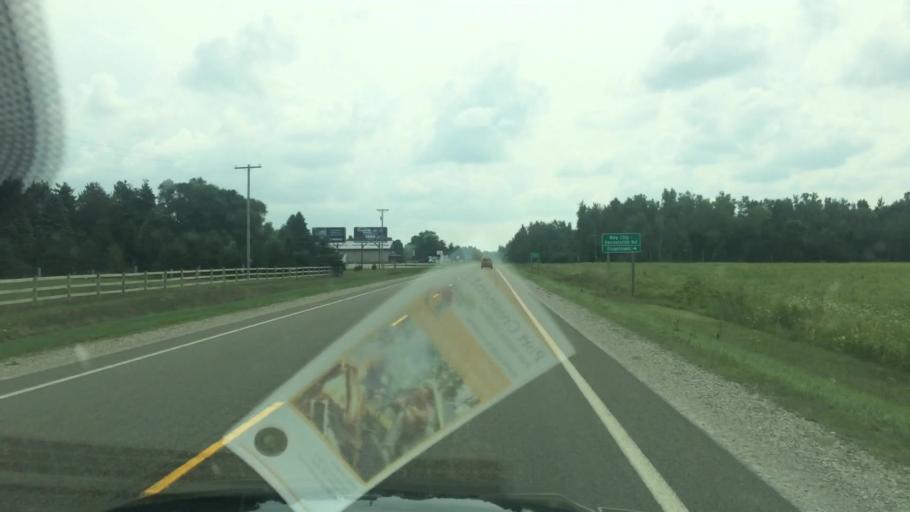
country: US
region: Michigan
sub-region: Tuscola County
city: Cass City
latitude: 43.6636
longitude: -83.0983
